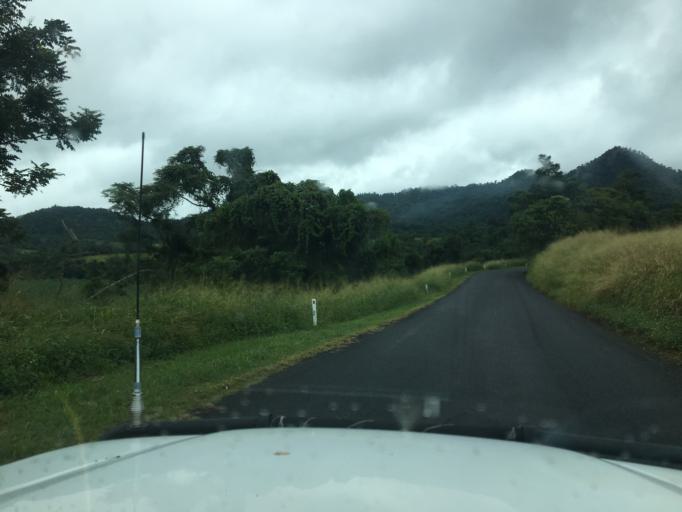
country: AU
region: Queensland
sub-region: Cassowary Coast
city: Innisfail
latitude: -17.4472
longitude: 145.8594
